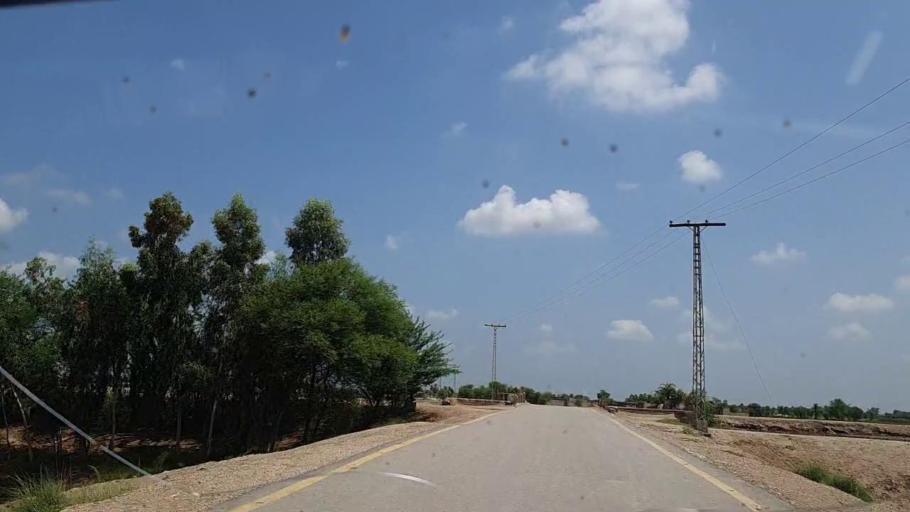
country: PK
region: Sindh
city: Tharu Shah
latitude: 26.9856
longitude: 68.0787
